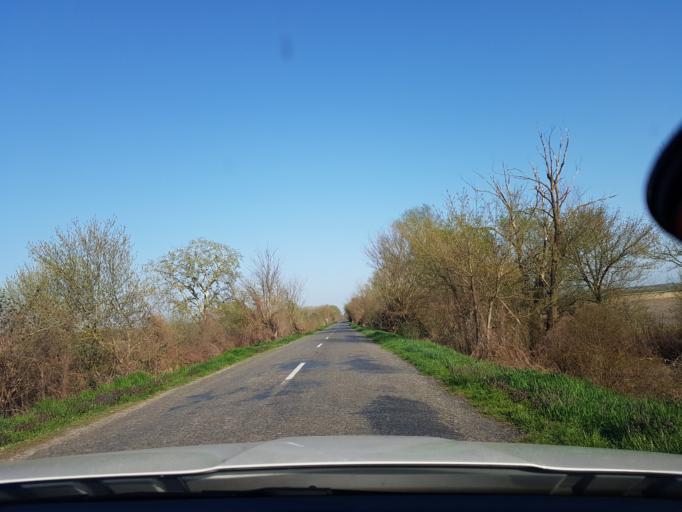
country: HU
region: Tolna
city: Bogyiszlo
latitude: 46.3321
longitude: 18.8225
